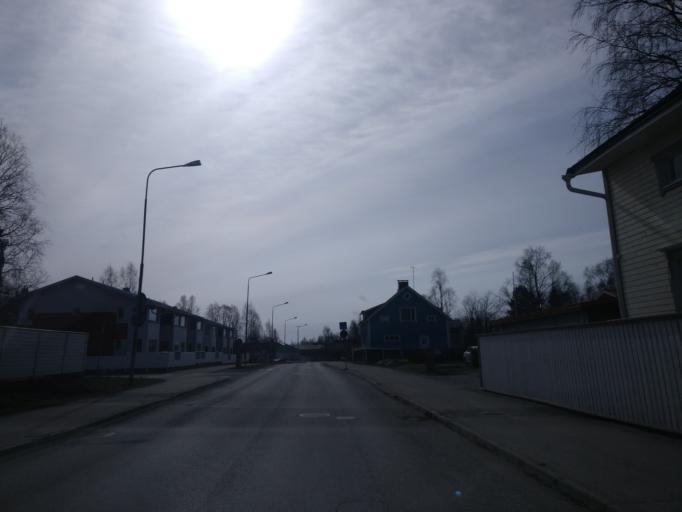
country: FI
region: Lapland
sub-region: Kemi-Tornio
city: Kemi
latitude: 65.7447
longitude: 24.5650
